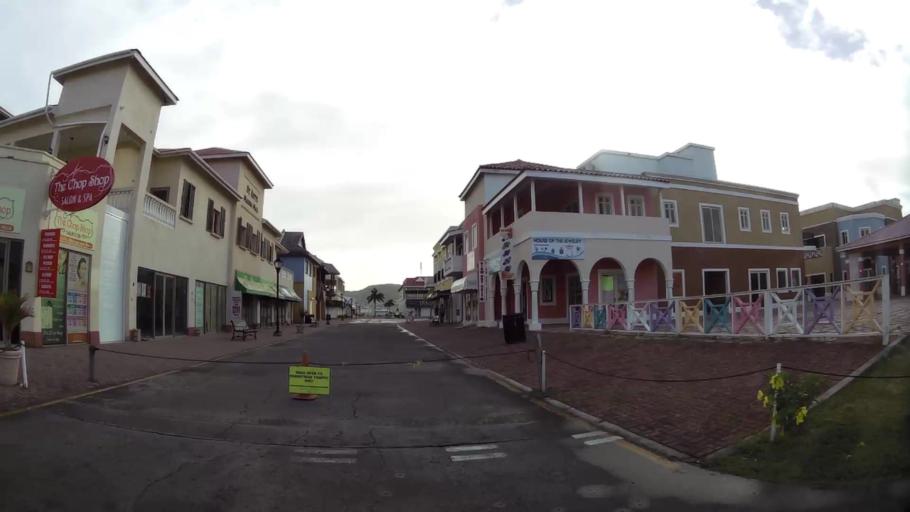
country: KN
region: Saint George Basseterre
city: Basseterre
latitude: 17.2927
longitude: -62.7235
